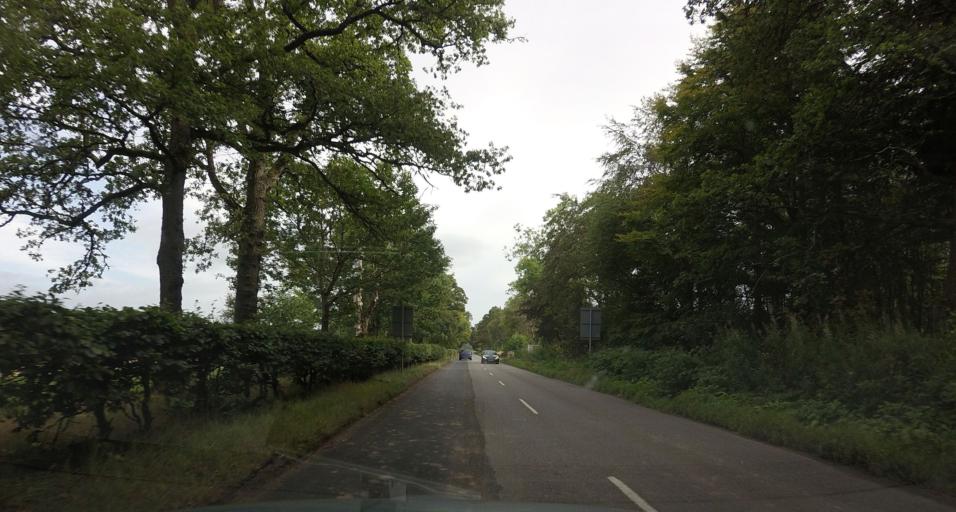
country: GB
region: Scotland
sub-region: Aberdeenshire
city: Kemnay
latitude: 57.2242
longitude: -2.5206
